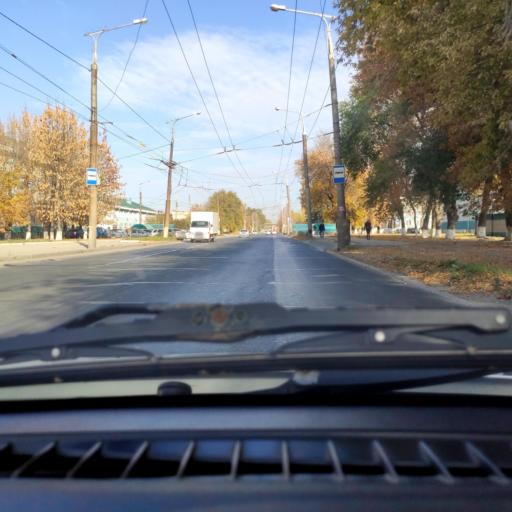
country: RU
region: Samara
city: Tol'yatti
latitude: 53.5401
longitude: 49.4430
